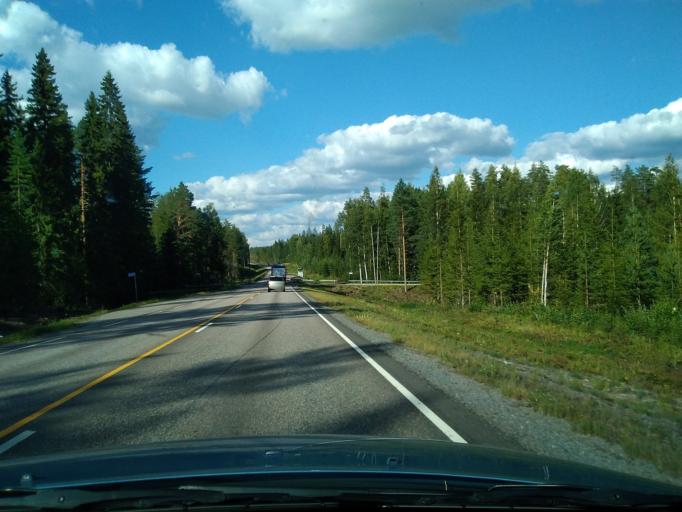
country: FI
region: Central Finland
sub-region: Keuruu
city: Keuruu
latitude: 62.1369
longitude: 24.7404
